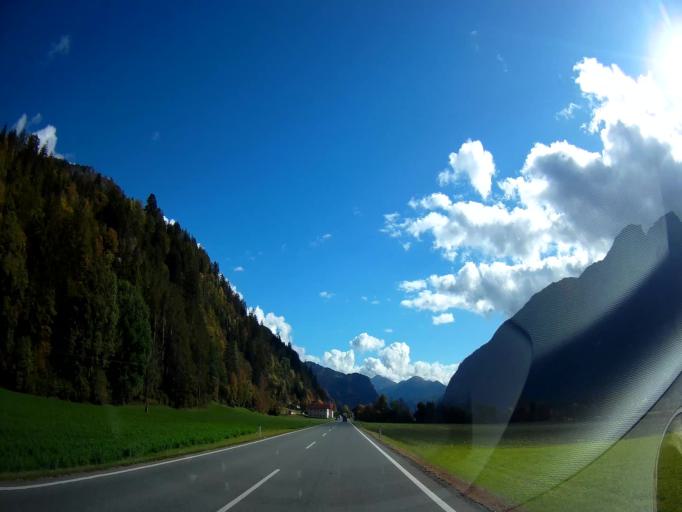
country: AT
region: Tyrol
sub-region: Politischer Bezirk Lienz
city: Lavant
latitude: 46.8103
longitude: 12.8509
